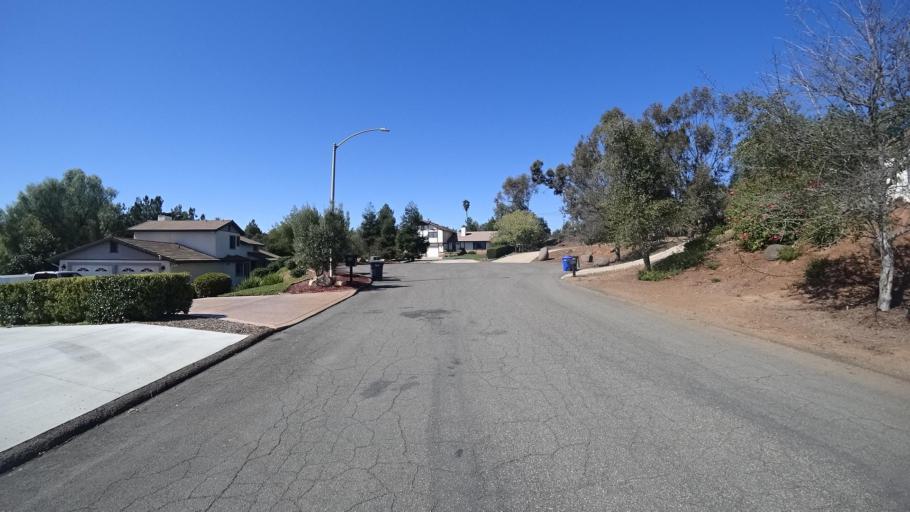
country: US
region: California
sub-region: San Diego County
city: Alpine
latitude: 32.8149
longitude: -116.7795
